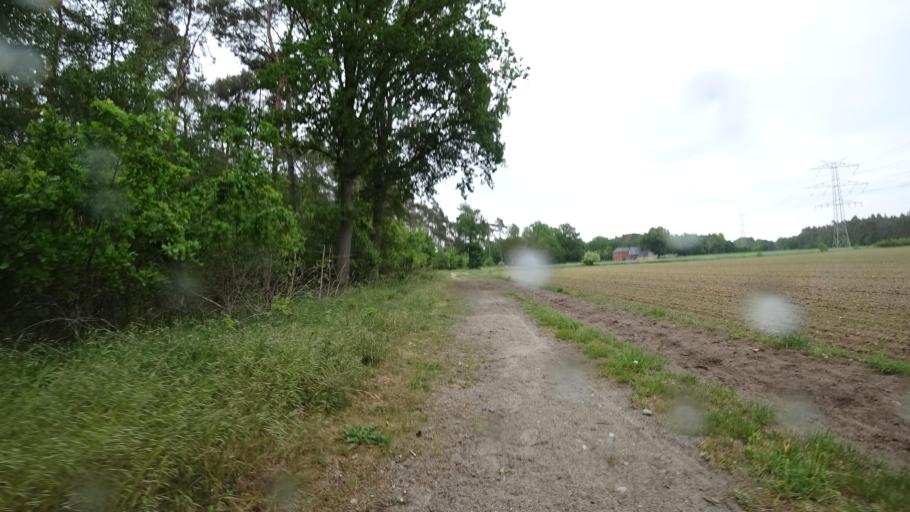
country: DE
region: North Rhine-Westphalia
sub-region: Regierungsbezirk Detmold
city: Rheda-Wiedenbruck
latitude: 51.9073
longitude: 8.2929
